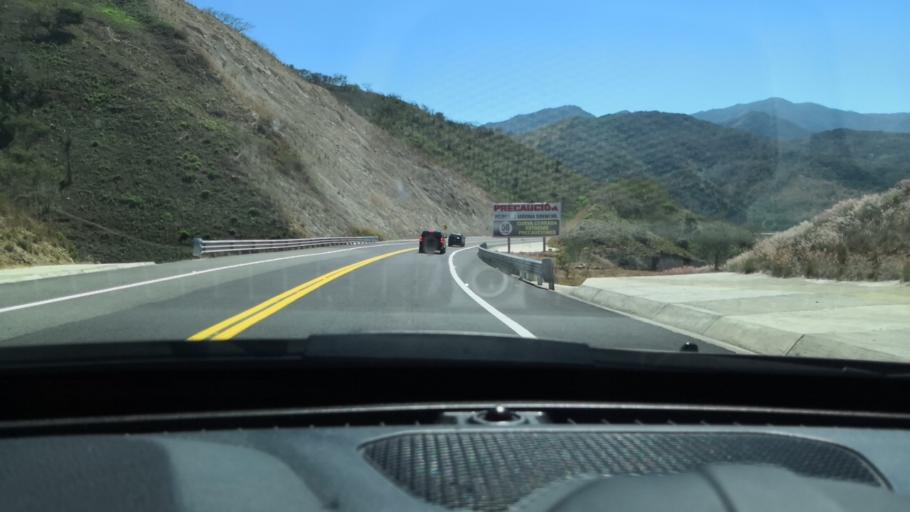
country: MX
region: Nayarit
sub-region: Compostela
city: Juan Escutia (Borbollon)
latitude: 21.1417
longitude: -104.9098
